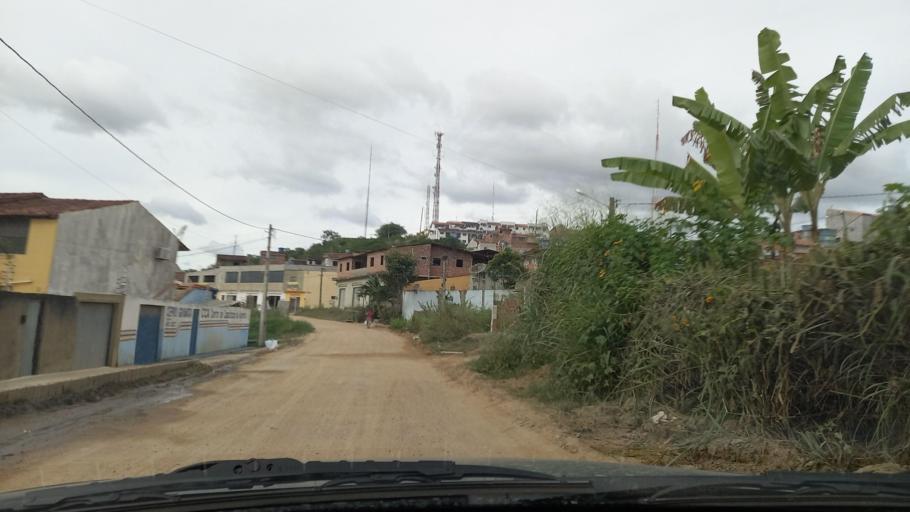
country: BR
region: Pernambuco
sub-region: Gravata
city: Gravata
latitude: -8.2126
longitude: -35.5776
